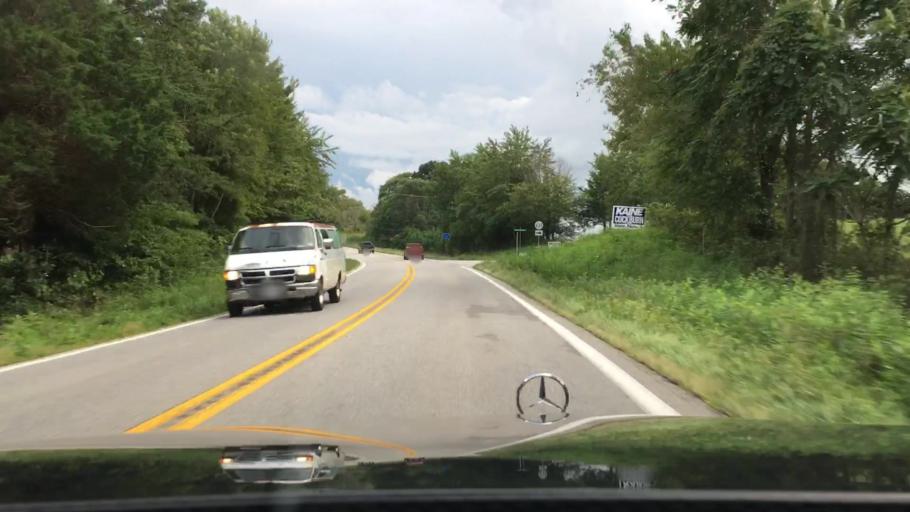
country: US
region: Virginia
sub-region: Nelson County
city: Nellysford
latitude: 37.9376
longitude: -78.8408
